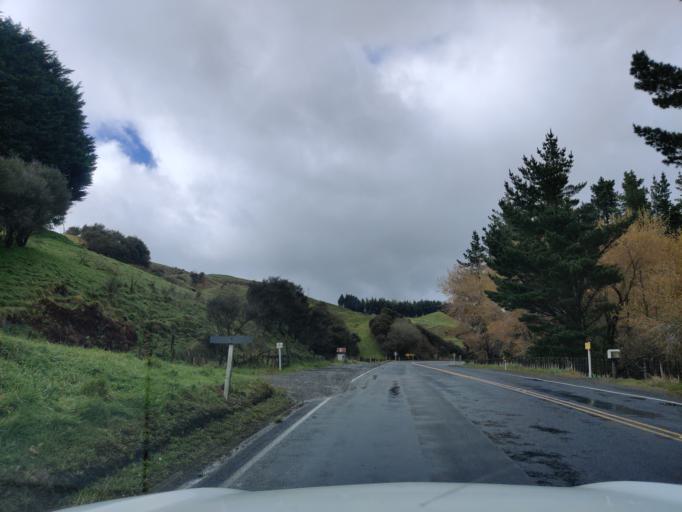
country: NZ
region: Waikato
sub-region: Otorohanga District
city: Otorohanga
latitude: -38.6379
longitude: 175.2054
